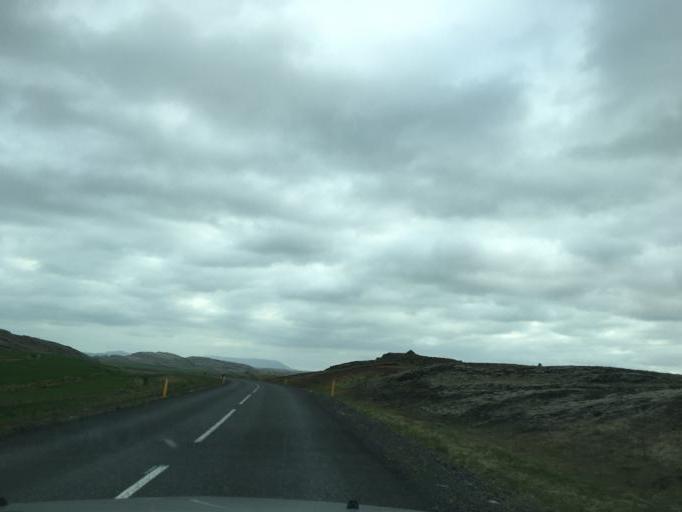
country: IS
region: South
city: Vestmannaeyjar
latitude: 64.2311
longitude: -20.2444
